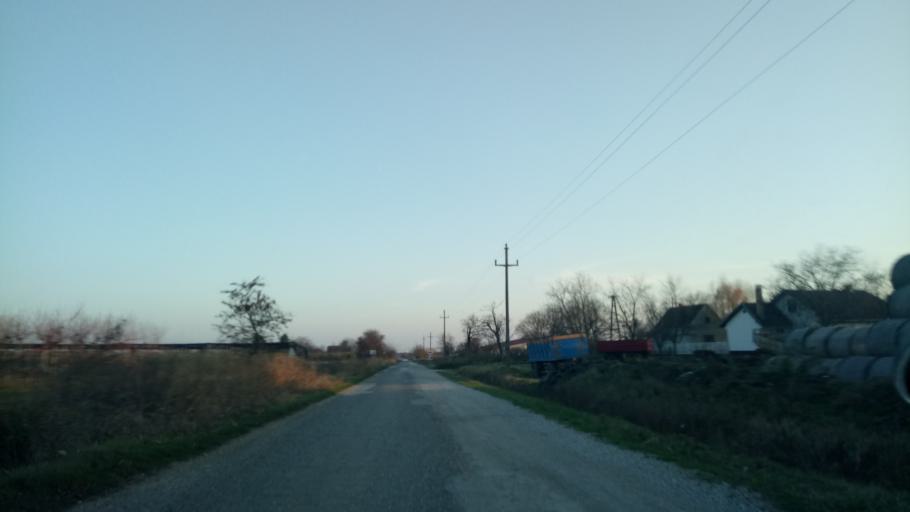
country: RS
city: Novi Slankamen
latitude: 45.1312
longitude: 20.2554
